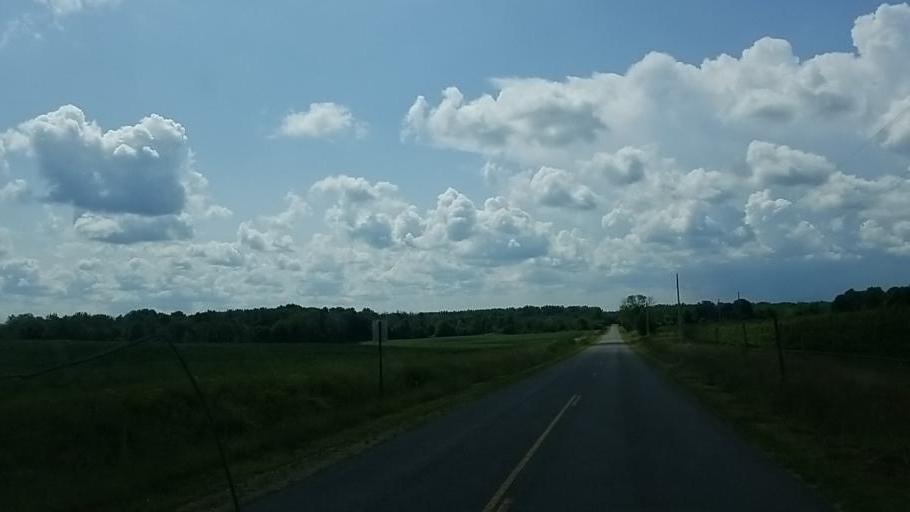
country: US
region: Michigan
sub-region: Muskegon County
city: Ravenna
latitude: 43.2188
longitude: -85.8799
